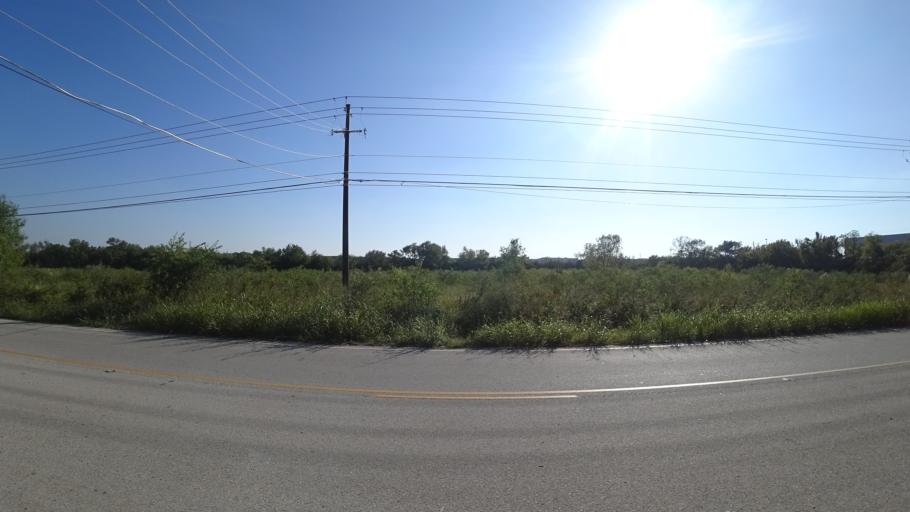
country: US
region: Texas
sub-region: Travis County
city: Wells Branch
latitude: 30.3429
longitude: -97.6653
